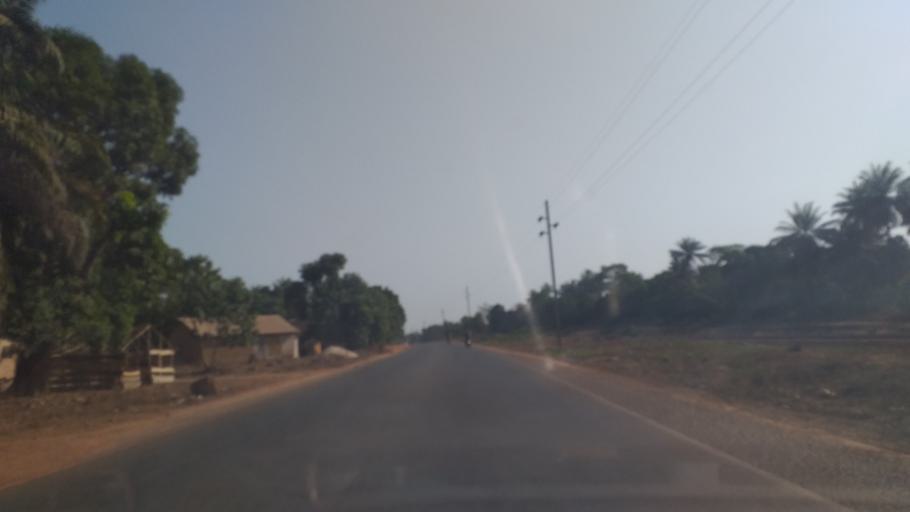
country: GN
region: Boke
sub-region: Boke Prefecture
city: Kamsar
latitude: 10.7434
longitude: -14.5115
